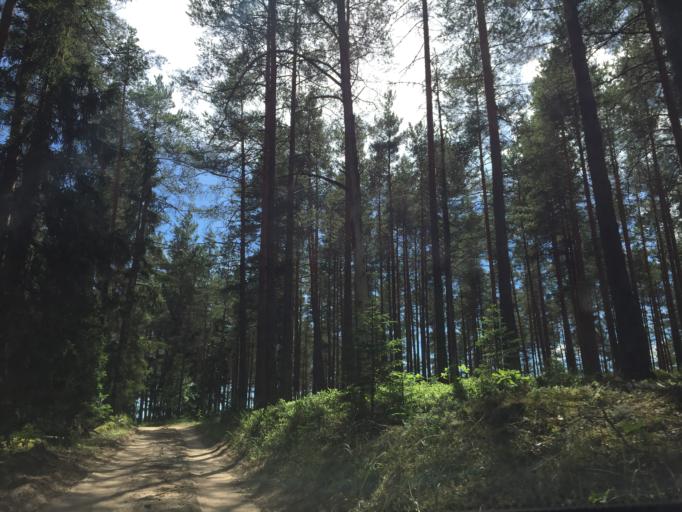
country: LV
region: Kuldigas Rajons
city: Kuldiga
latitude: 57.1121
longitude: 21.8774
